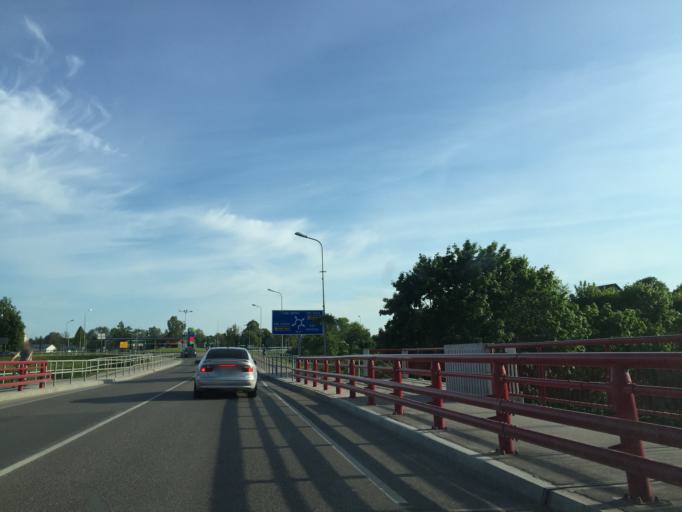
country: LV
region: Bauskas Rajons
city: Bauska
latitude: 56.4015
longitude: 24.1777
